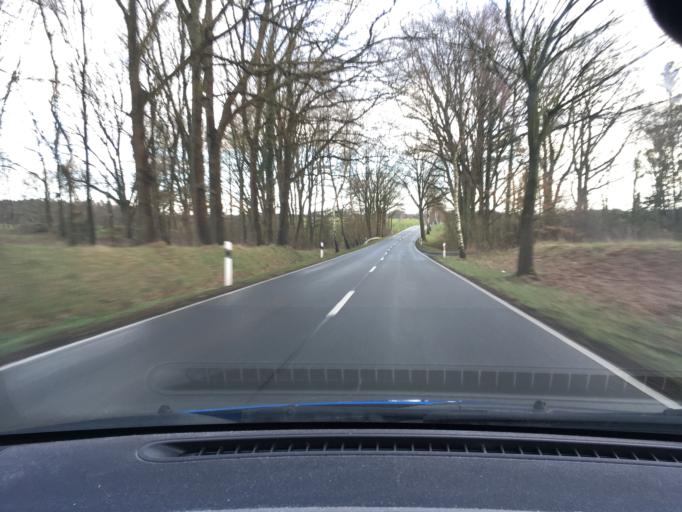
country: DE
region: Lower Saxony
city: Hanstedt
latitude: 53.2214
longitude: 10.0261
